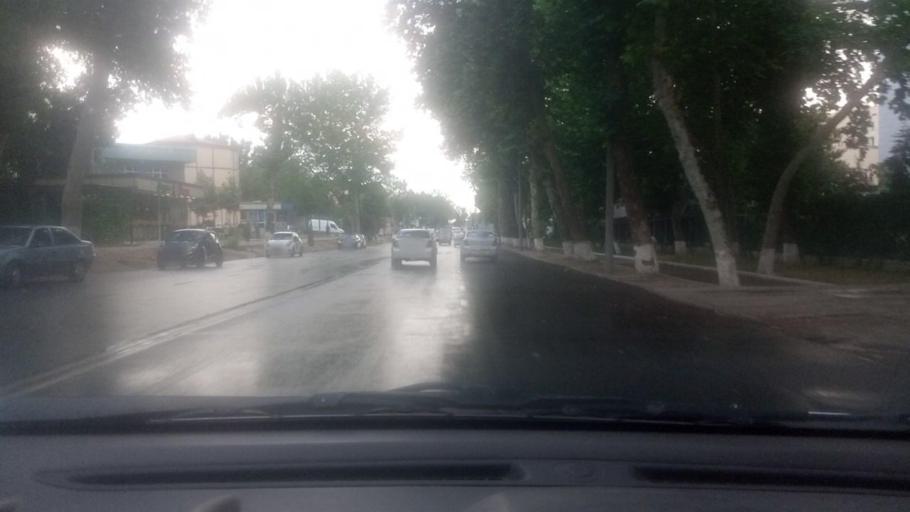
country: UZ
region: Toshkent Shahri
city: Tashkent
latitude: 41.2979
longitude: 69.1925
